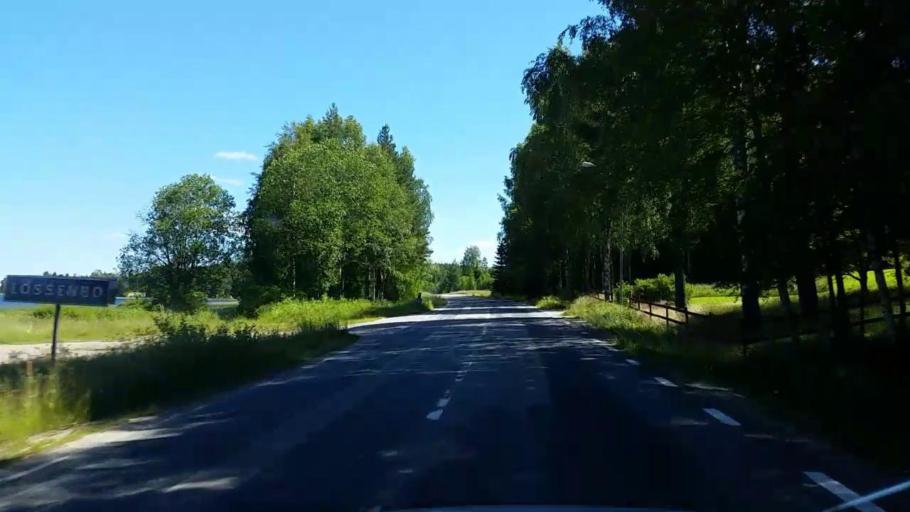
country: SE
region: Gaevleborg
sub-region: Ovanakers Kommun
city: Edsbyn
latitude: 61.3313
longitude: 15.8339
